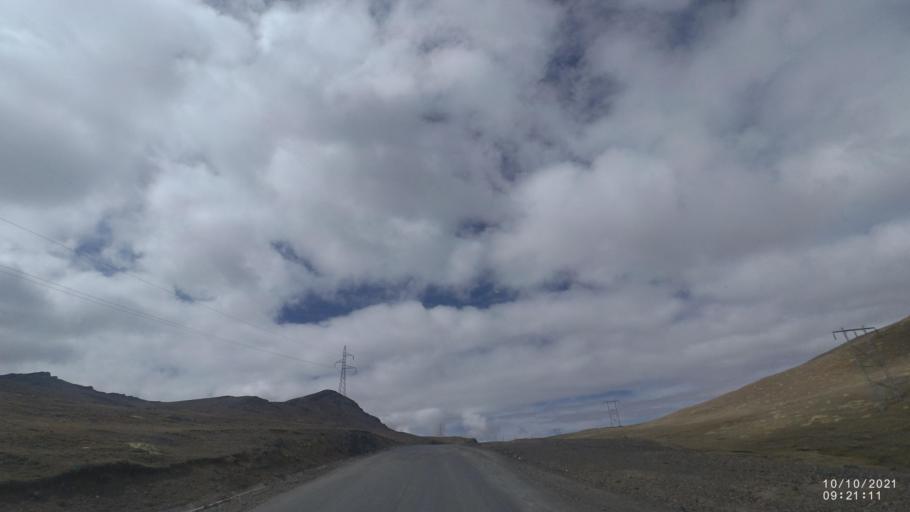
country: BO
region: La Paz
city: Quime
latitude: -17.0658
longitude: -67.2983
